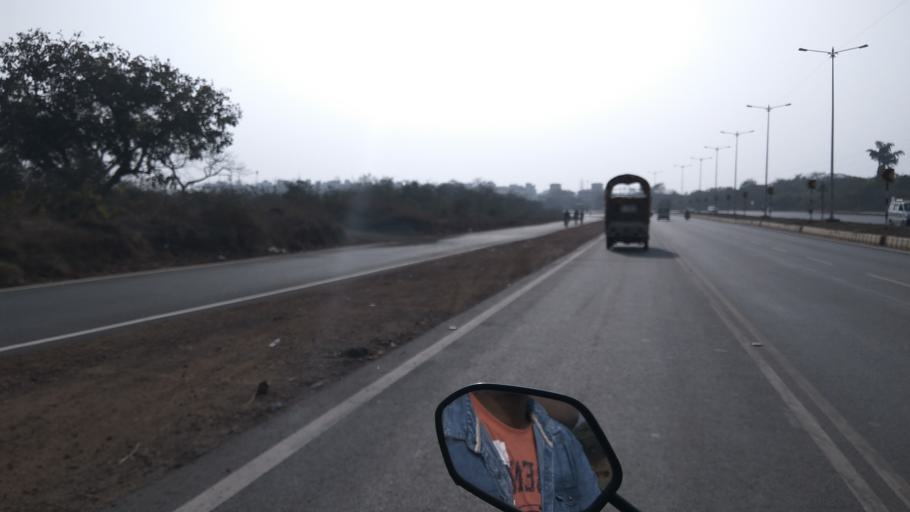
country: IN
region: Goa
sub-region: North Goa
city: Goa Velha
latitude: 15.4882
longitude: 73.8980
